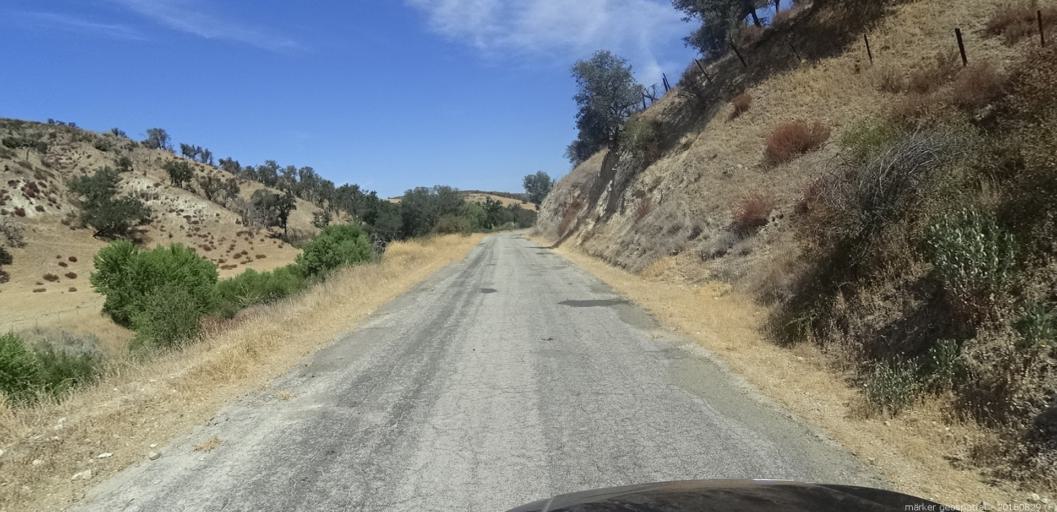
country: US
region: California
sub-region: San Luis Obispo County
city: Lake Nacimiento
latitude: 35.8546
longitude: -121.0358
